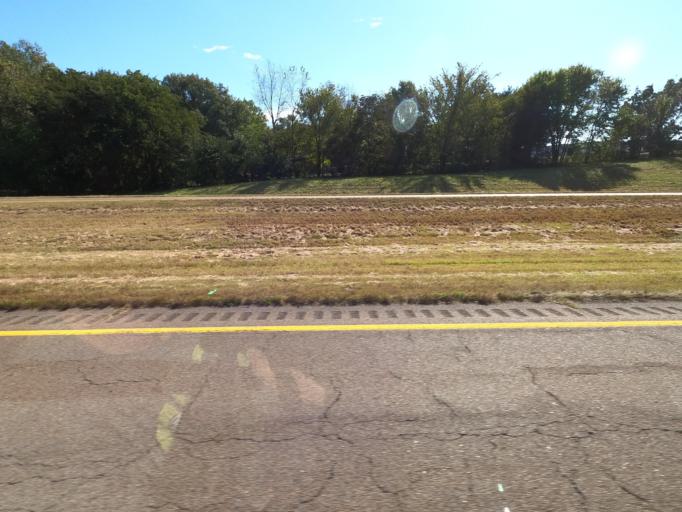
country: US
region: Tennessee
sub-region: Obion County
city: South Fulton
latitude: 36.4950
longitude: -88.9115
